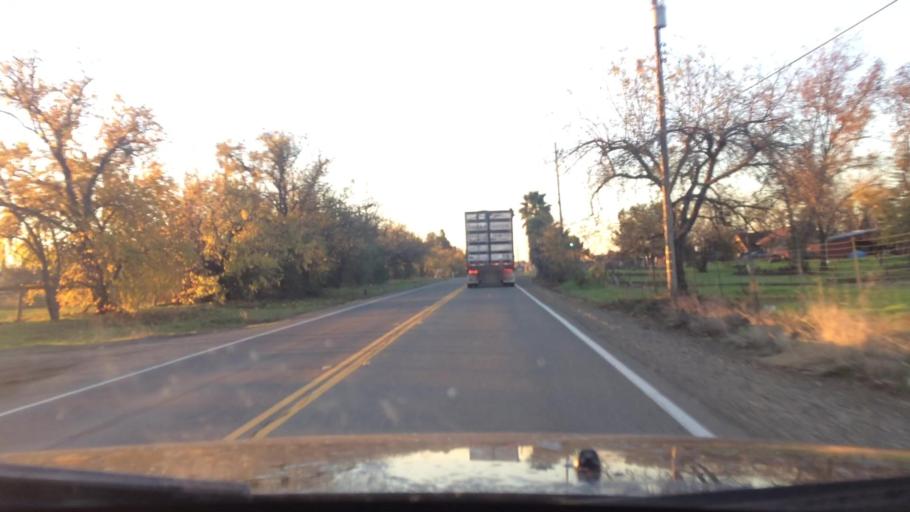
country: US
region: California
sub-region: Sacramento County
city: Vineyard
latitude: 38.5145
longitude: -121.2980
